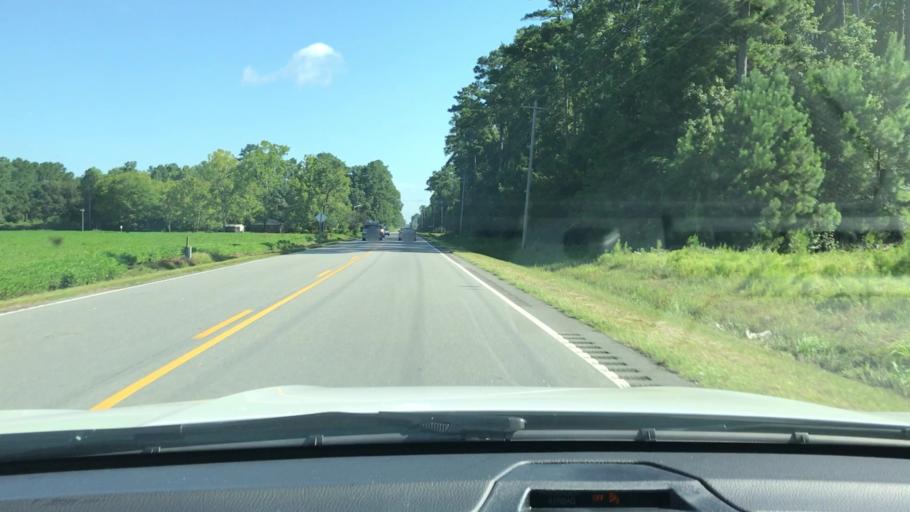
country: US
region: South Carolina
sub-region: Horry County
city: Socastee
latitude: 33.7254
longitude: -79.0850
